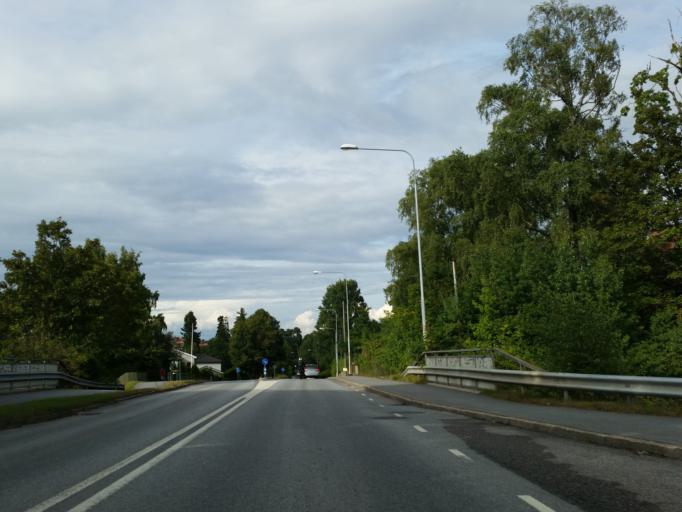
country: SE
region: Stockholm
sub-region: Sollentuna Kommun
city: Sollentuna
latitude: 59.4353
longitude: 17.9501
